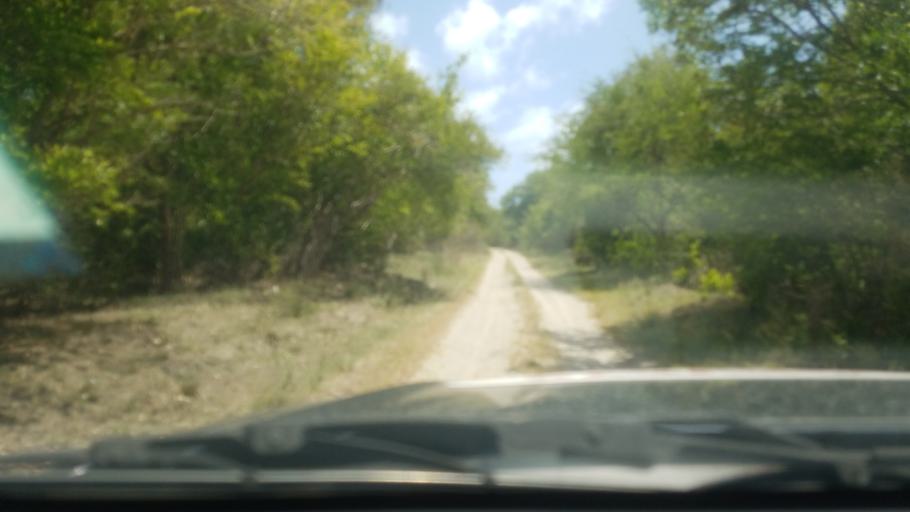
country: LC
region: Vieux-Fort
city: Vieux Fort
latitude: 13.7516
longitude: -60.9405
